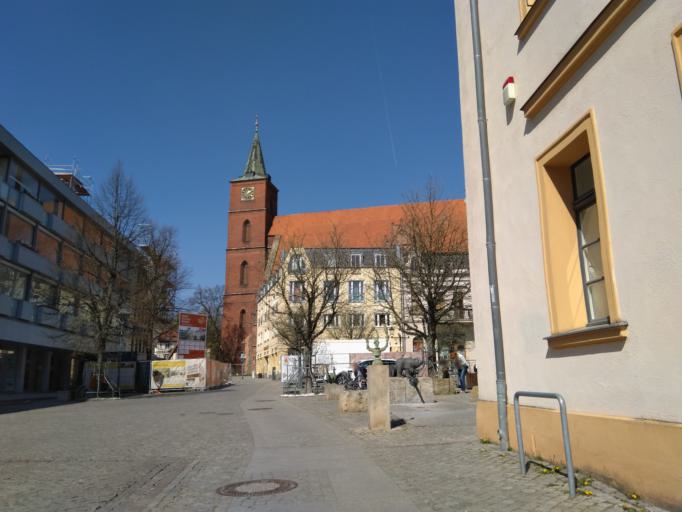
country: DE
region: Brandenburg
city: Bernau bei Berlin
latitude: 52.6788
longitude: 13.5876
